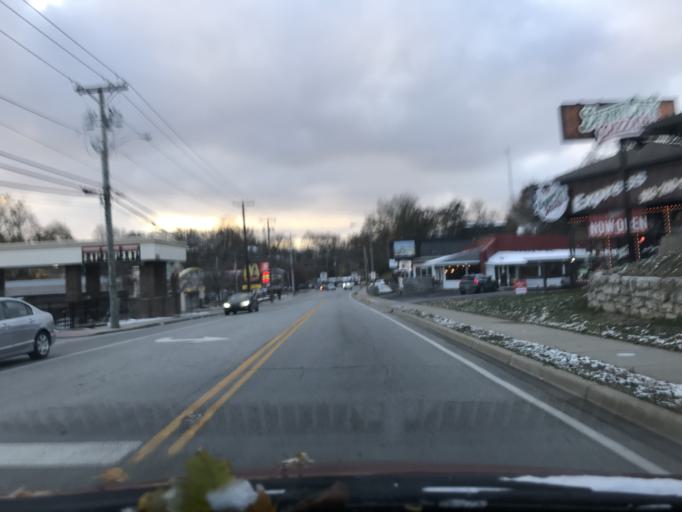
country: US
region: Indiana
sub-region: Clark County
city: Jeffersonville
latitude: 38.2583
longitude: -85.7018
